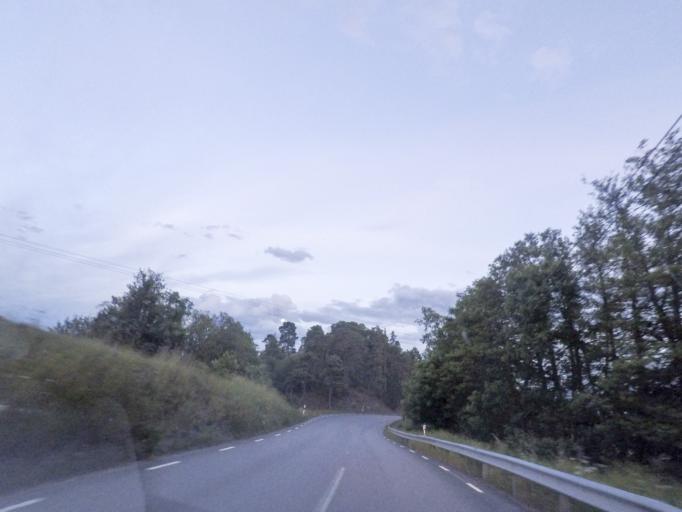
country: SE
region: Uppsala
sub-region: Habo Kommun
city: Balsta
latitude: 59.6295
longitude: 17.5001
